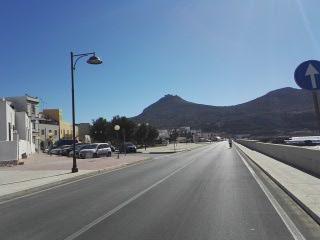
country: IT
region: Sicily
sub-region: Trapani
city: Favignana
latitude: 37.9341
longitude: 12.3311
